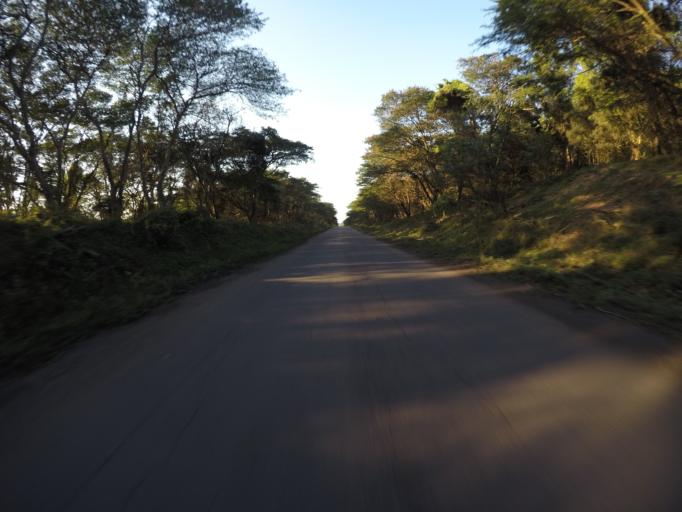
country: ZA
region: KwaZulu-Natal
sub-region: uThungulu District Municipality
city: KwaMbonambi
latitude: -28.6980
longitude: 32.2073
